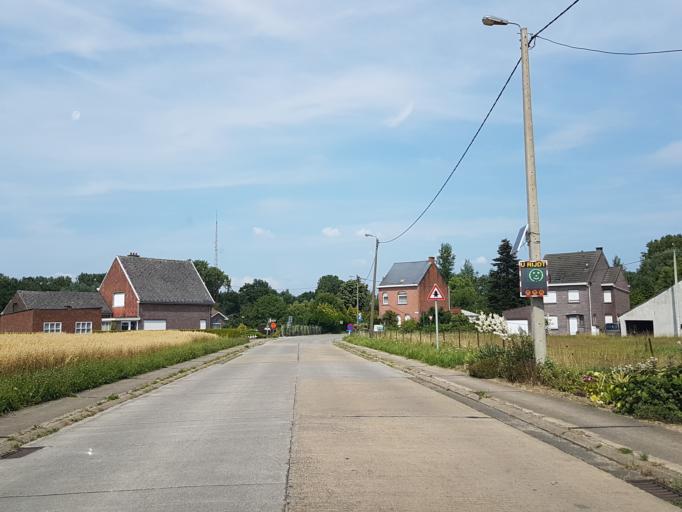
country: BE
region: Flanders
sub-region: Provincie Vlaams-Brabant
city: Kampenhout
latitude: 50.9274
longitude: 4.5659
